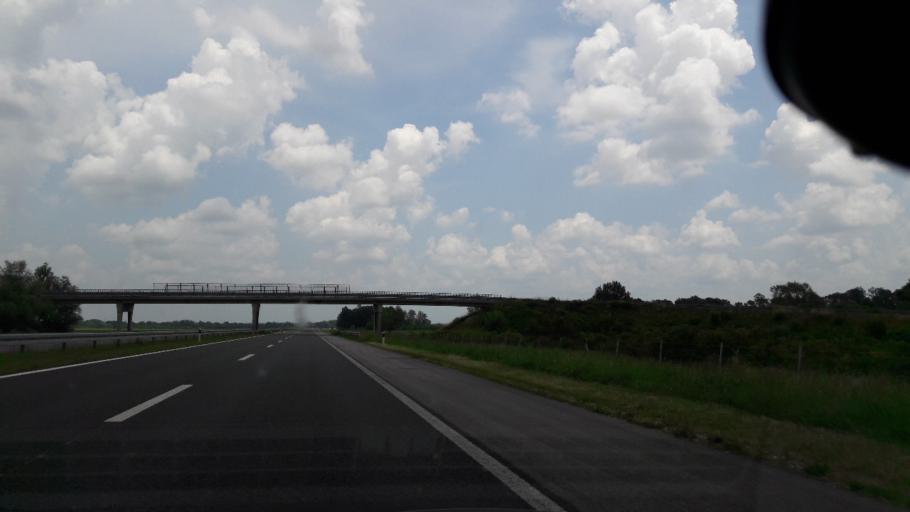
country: HR
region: Vukovarsko-Srijemska
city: Stitar
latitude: 45.1107
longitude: 18.6525
